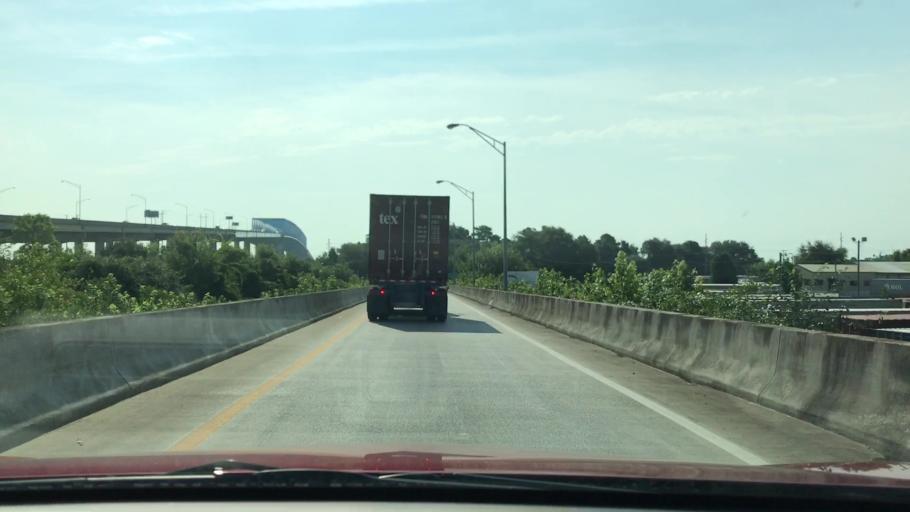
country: US
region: South Carolina
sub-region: Charleston County
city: North Charleston
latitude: 32.8923
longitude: -79.9758
